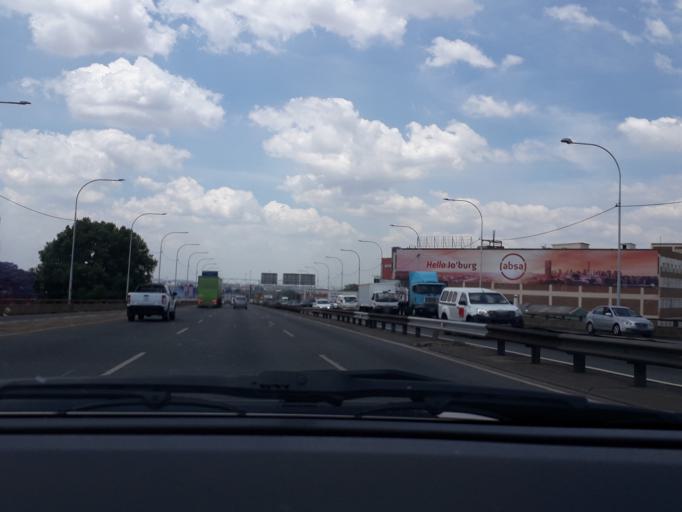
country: ZA
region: Gauteng
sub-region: City of Johannesburg Metropolitan Municipality
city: Johannesburg
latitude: -26.2129
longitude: 28.0457
